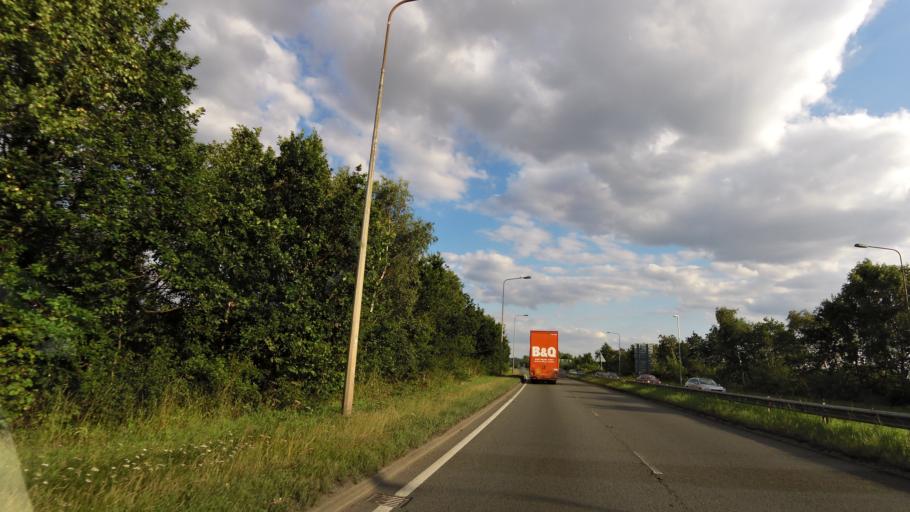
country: GB
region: England
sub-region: Nottinghamshire
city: Worksop
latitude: 53.3102
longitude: -1.1418
